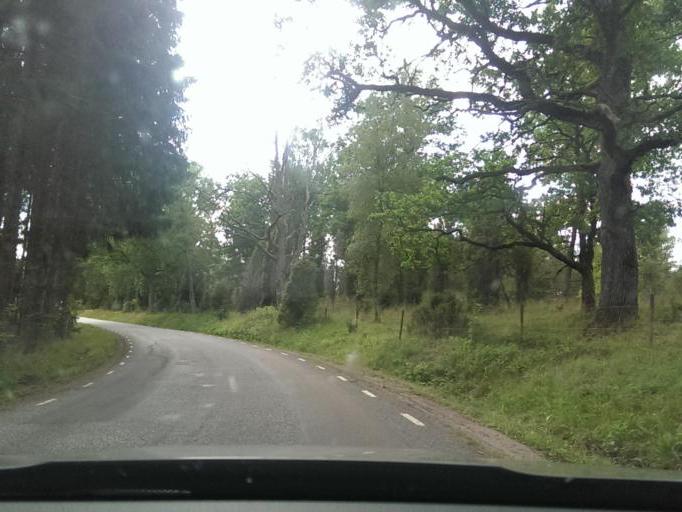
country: SE
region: Kronoberg
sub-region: Ljungby Kommun
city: Lagan
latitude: 56.9954
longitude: 13.9381
